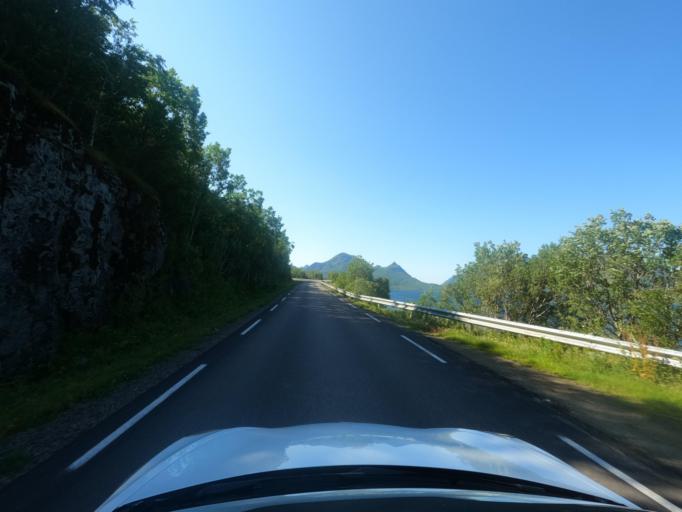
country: NO
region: Nordland
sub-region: Hadsel
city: Stokmarknes
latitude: 68.3263
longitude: 15.0092
